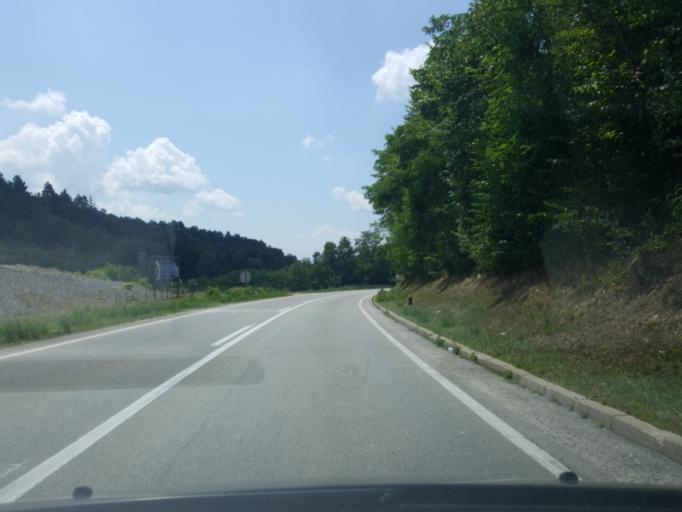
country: RS
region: Central Serbia
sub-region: Moravicki Okrug
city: Gornji Milanovac
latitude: 44.1063
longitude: 20.4834
